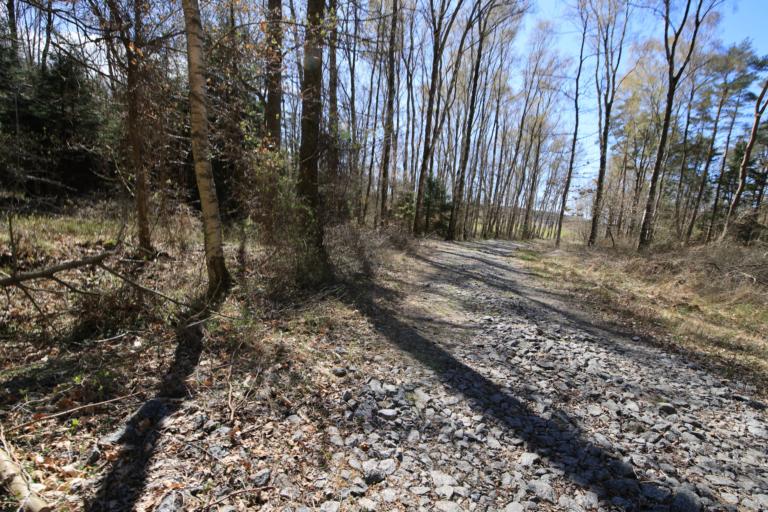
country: SE
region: Halland
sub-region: Varbergs Kommun
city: Varberg
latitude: 57.1877
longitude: 12.2306
